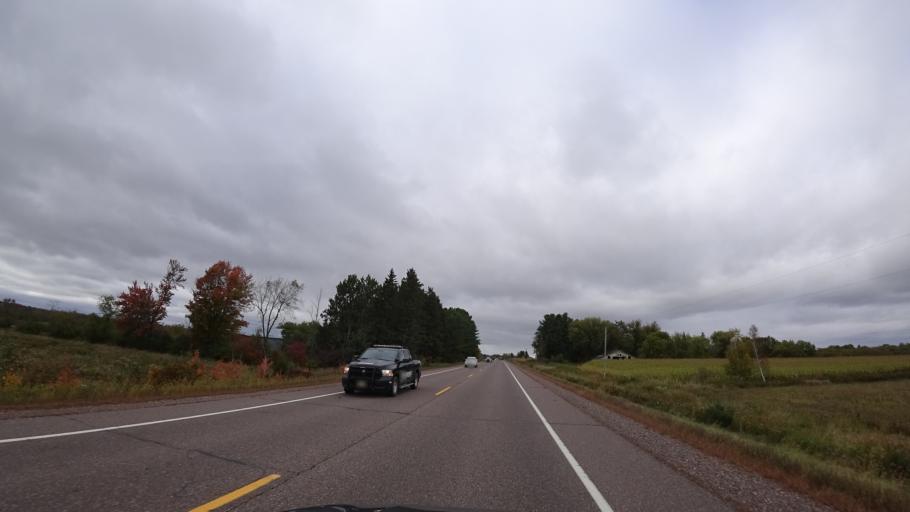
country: US
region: Wisconsin
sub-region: Rusk County
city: Ladysmith
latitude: 45.5406
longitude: -91.1114
